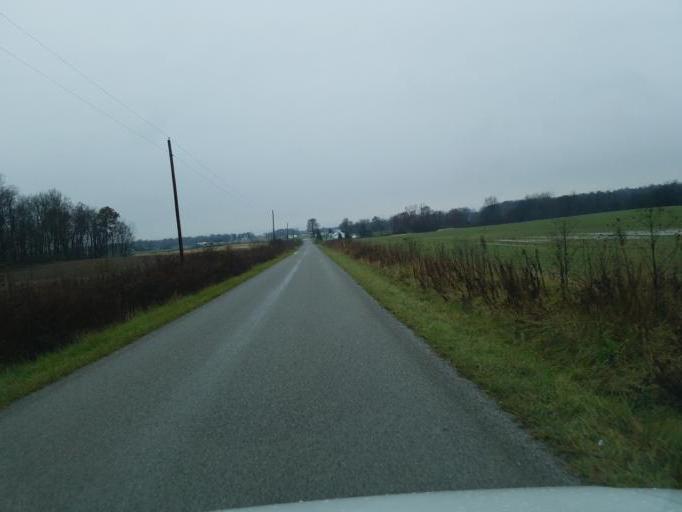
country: US
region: Ohio
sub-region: Knox County
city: Centerburg
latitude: 40.3716
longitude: -82.6660
